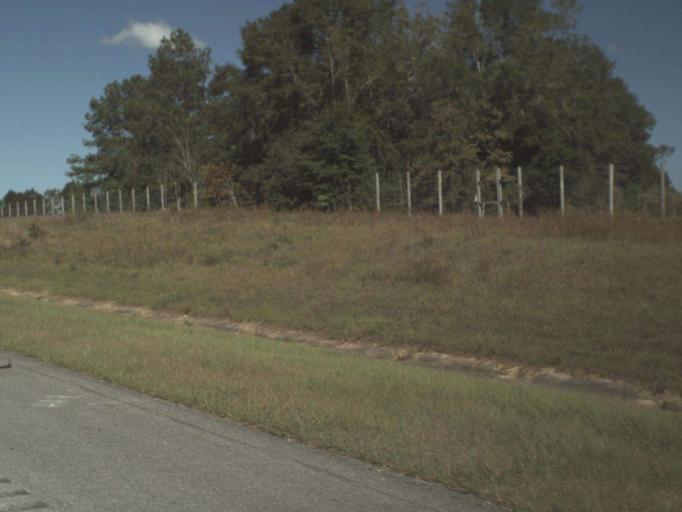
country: US
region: Florida
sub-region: Jackson County
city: Marianna
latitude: 30.6927
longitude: -85.1213
